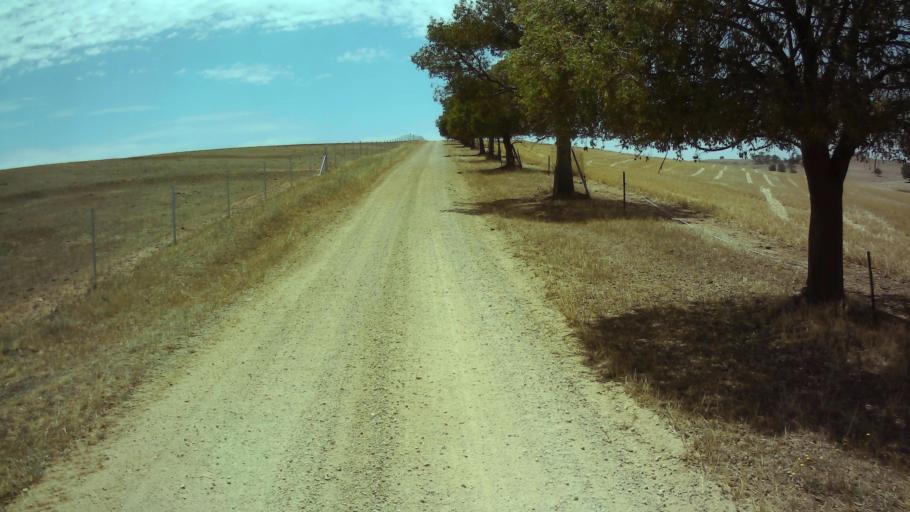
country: AU
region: New South Wales
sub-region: Cowra
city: Cowra
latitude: -33.9584
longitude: 148.4530
